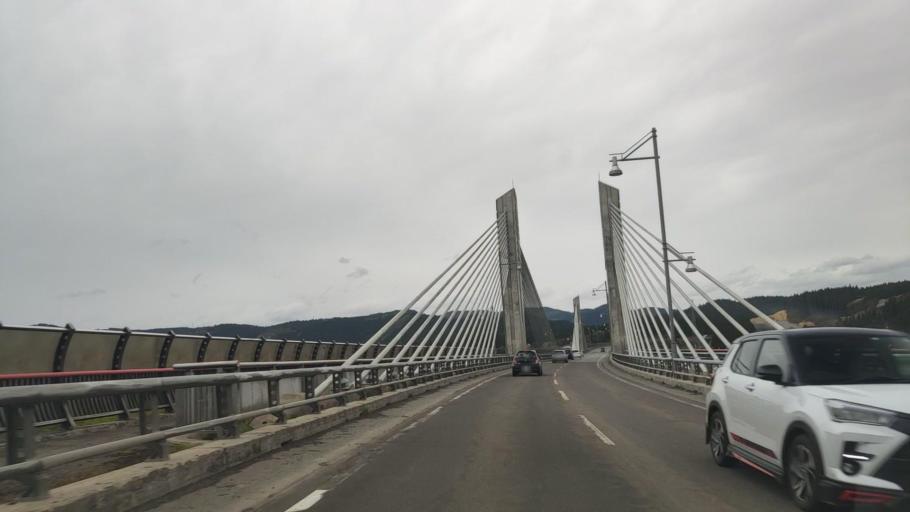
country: JP
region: Akita
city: Takanosu
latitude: 40.2059
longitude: 140.3043
